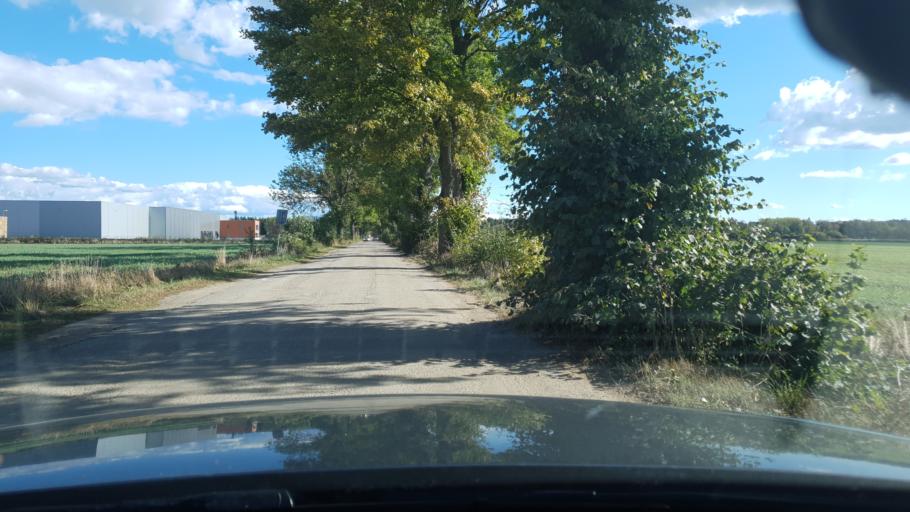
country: PL
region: Pomeranian Voivodeship
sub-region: Powiat pucki
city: Zelistrzewo
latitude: 54.6869
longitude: 18.4489
